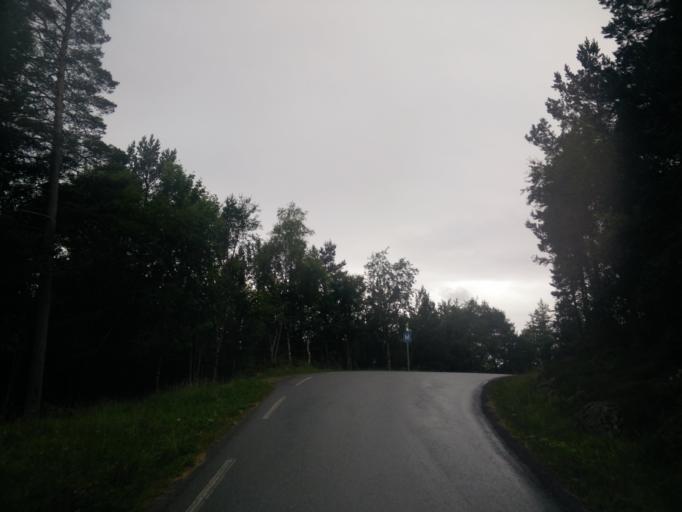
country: NO
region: More og Romsdal
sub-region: Kristiansund
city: Rensvik
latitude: 63.0218
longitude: 7.8968
